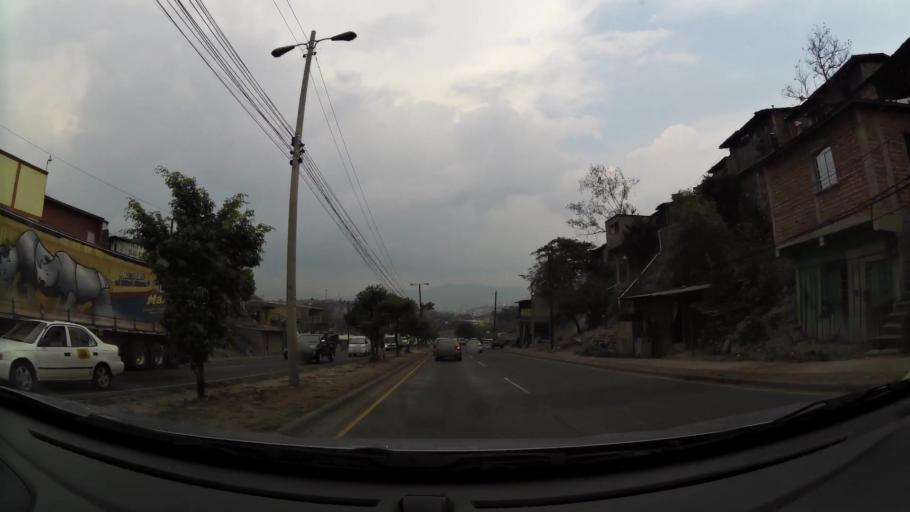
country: HN
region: Francisco Morazan
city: Tegucigalpa
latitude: 14.0852
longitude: -87.2239
